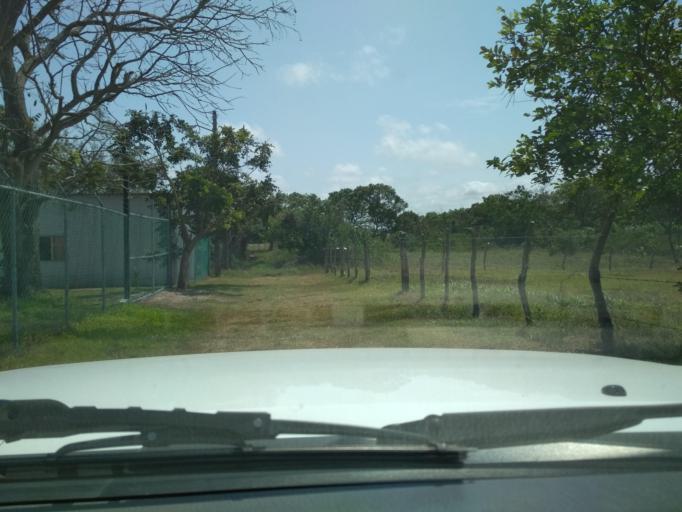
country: MX
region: Veracruz
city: Anton Lizardo
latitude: 19.0015
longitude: -95.9922
